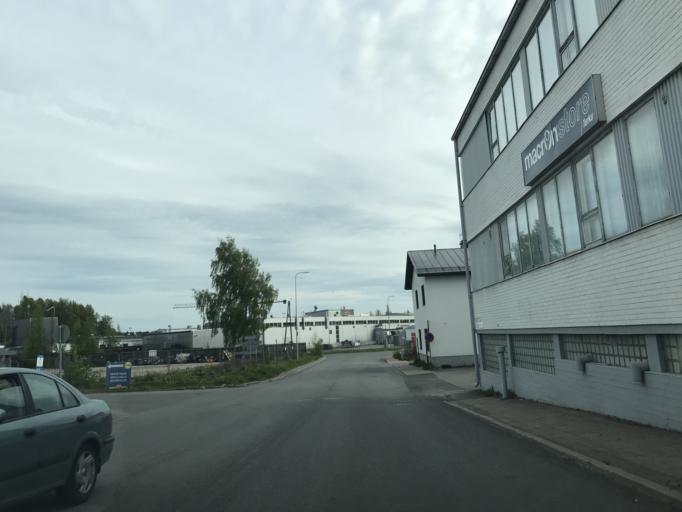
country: FI
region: Varsinais-Suomi
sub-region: Turku
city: Turku
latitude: 60.4496
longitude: 22.3084
